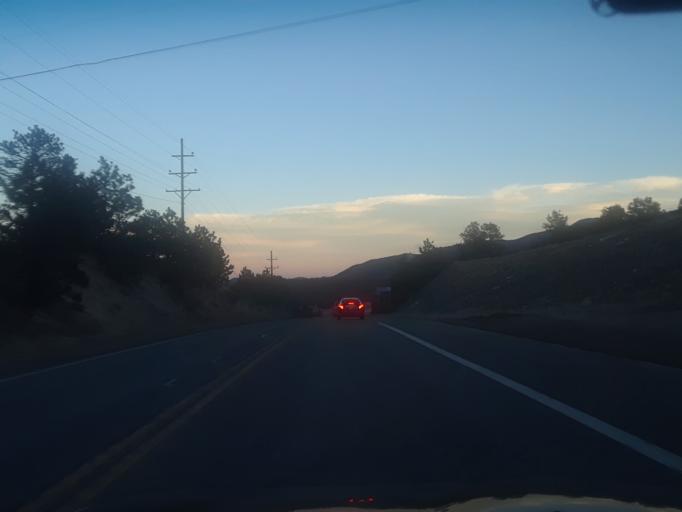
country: US
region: Colorado
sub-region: Clear Creek County
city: Georgetown
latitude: 39.4275
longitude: -105.5669
